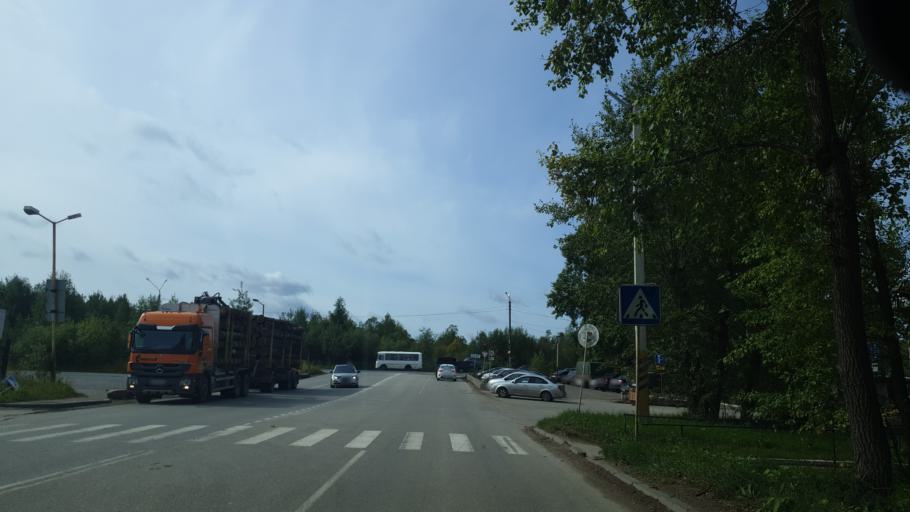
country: RU
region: Komi Republic
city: Ezhva
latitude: 61.8078
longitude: 50.7286
